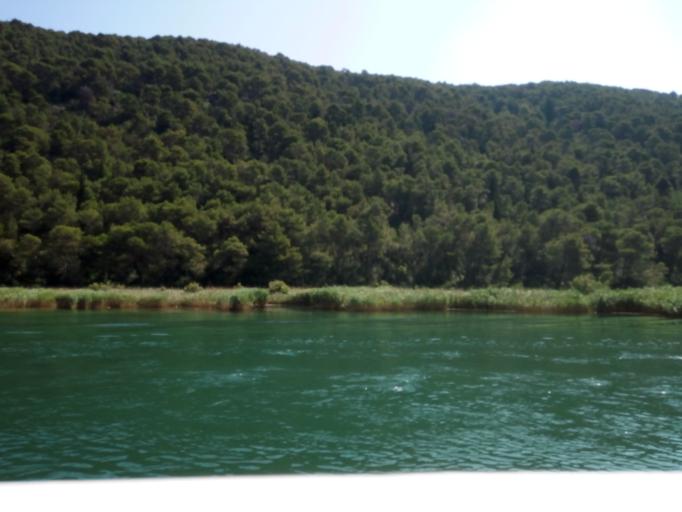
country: HR
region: Sibensko-Kniniska
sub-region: Grad Sibenik
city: Sibenik
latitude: 43.8155
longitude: 15.9509
